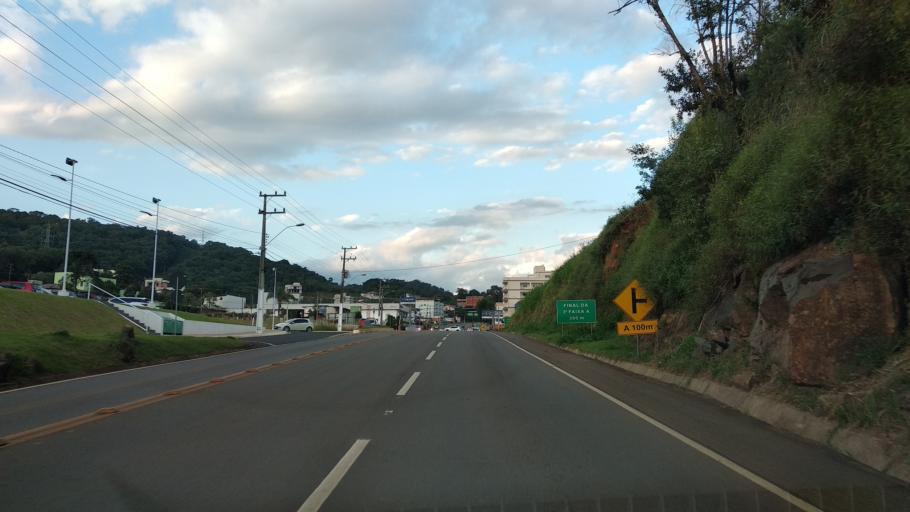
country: BR
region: Santa Catarina
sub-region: Videira
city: Videira
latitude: -27.0012
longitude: -51.1223
